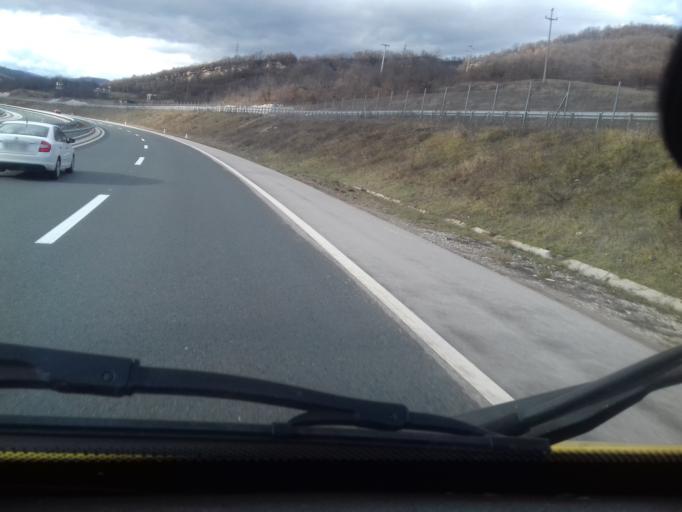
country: BA
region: Federation of Bosnia and Herzegovina
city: Kakanj
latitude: 44.1370
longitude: 18.0342
